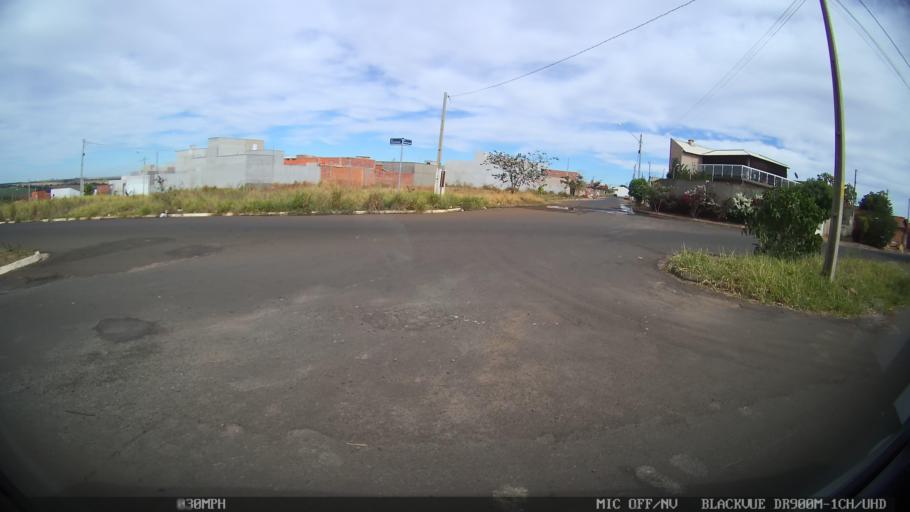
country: BR
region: Sao Paulo
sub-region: Catanduva
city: Catanduva
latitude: -21.1650
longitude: -48.9639
